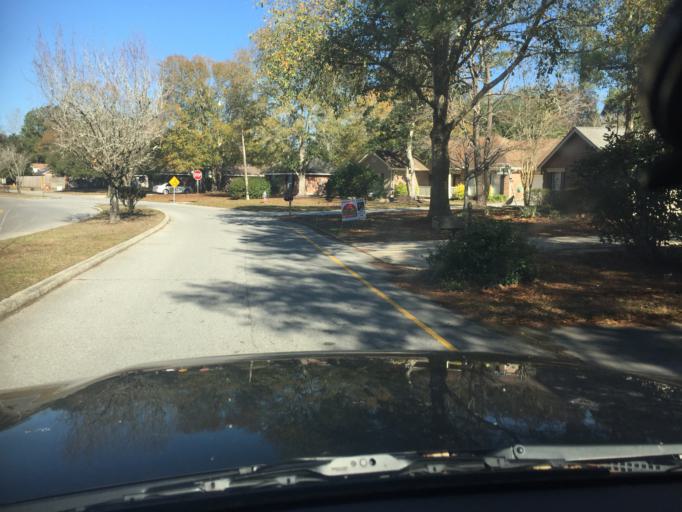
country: US
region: Louisiana
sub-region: Saint Tammany Parish
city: Slidell
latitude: 30.2988
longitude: -89.7240
